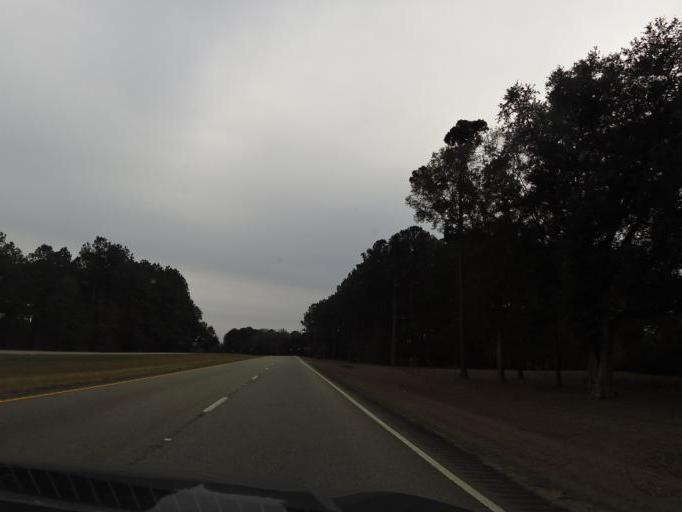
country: US
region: Georgia
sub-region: Thomas County
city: Thomasville
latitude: 30.7396
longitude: -83.9047
